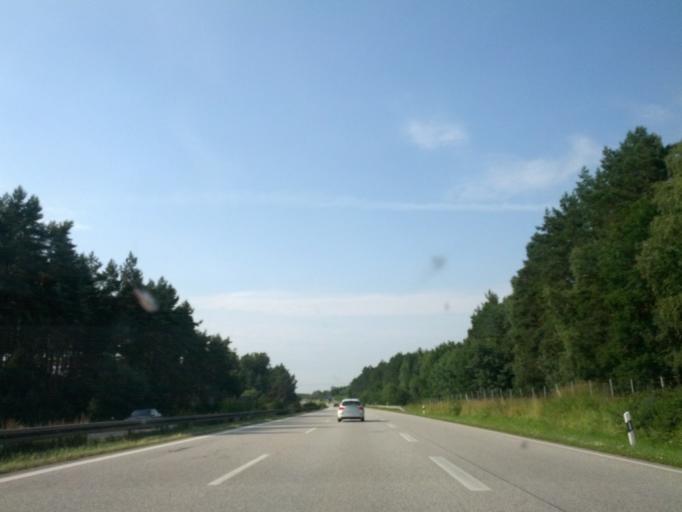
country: DE
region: Mecklenburg-Vorpommern
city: Lalendorf
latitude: 53.7778
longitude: 12.3181
